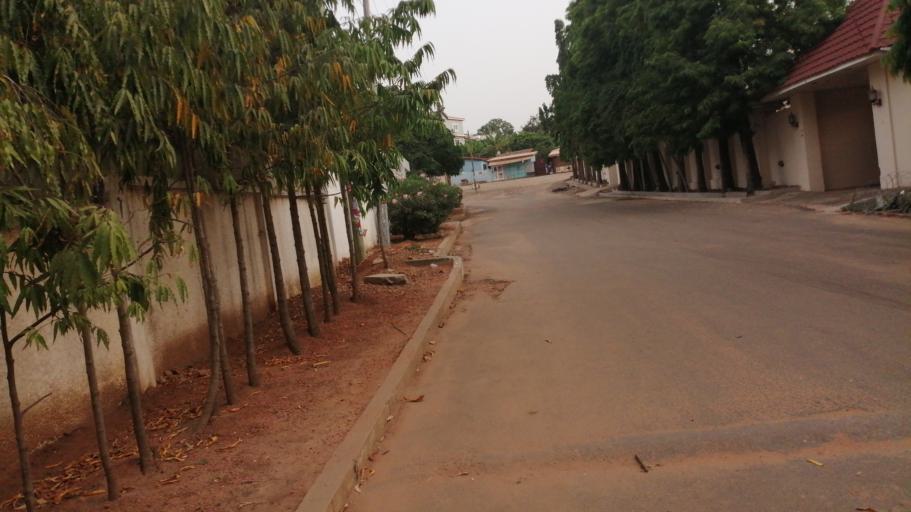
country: GH
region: Greater Accra
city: Medina Estates
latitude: 5.6190
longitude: -0.1795
